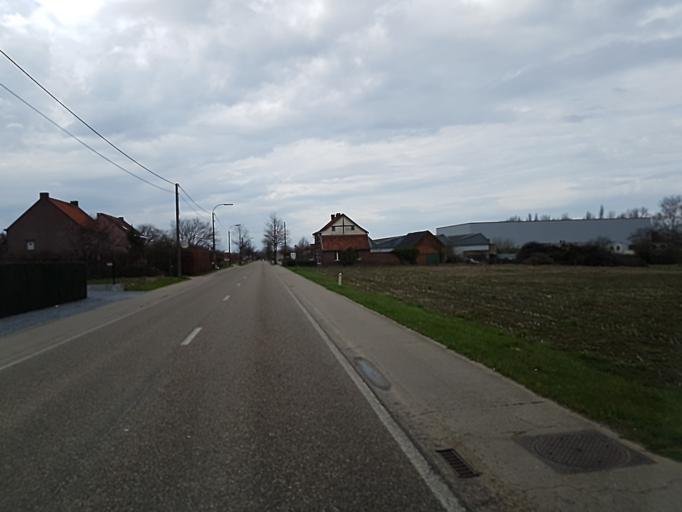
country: BE
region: Flanders
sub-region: Provincie Limburg
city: Nieuwerkerken
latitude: 50.9190
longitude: 5.2343
